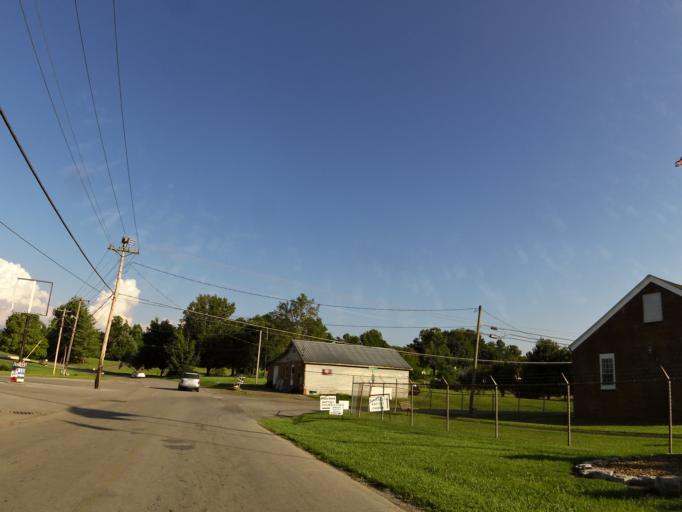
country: US
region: Tennessee
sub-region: Blount County
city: Maryville
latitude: 35.7147
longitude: -83.9214
